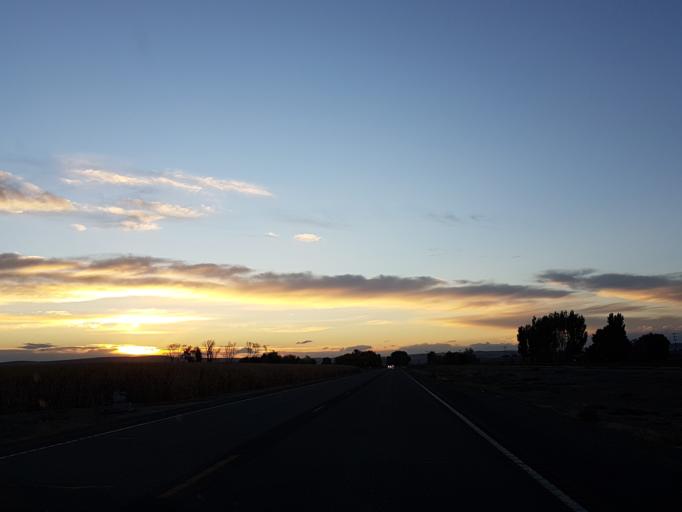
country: US
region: Oregon
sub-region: Malheur County
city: Vale
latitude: 43.9369
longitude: -117.3216
